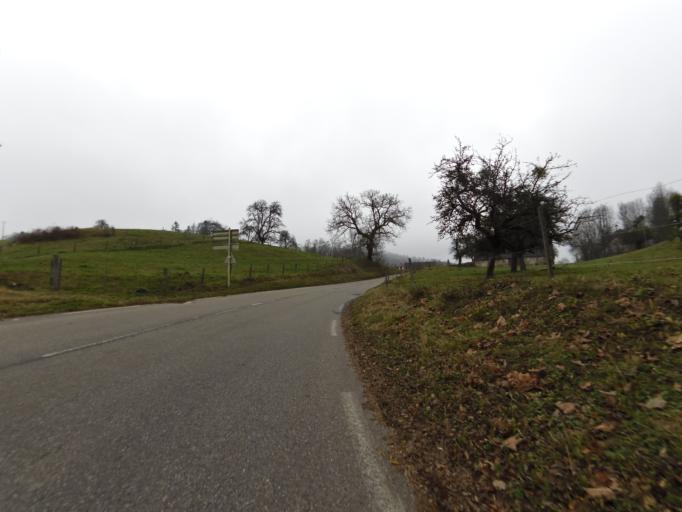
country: CH
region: Jura
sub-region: Delemont District
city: Bassecourt
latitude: 47.4262
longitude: 7.2462
